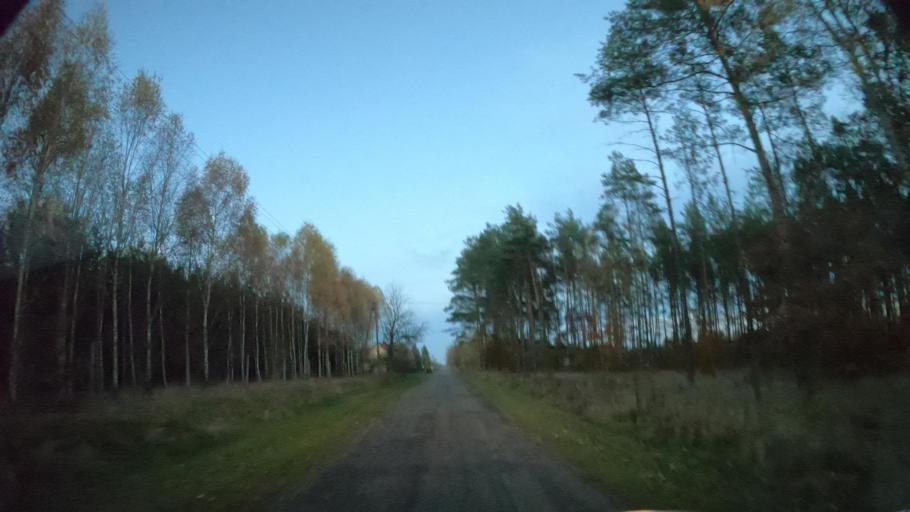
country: PL
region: Greater Poland Voivodeship
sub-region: Powiat zlotowski
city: Sypniewo
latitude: 53.4266
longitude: 16.6033
